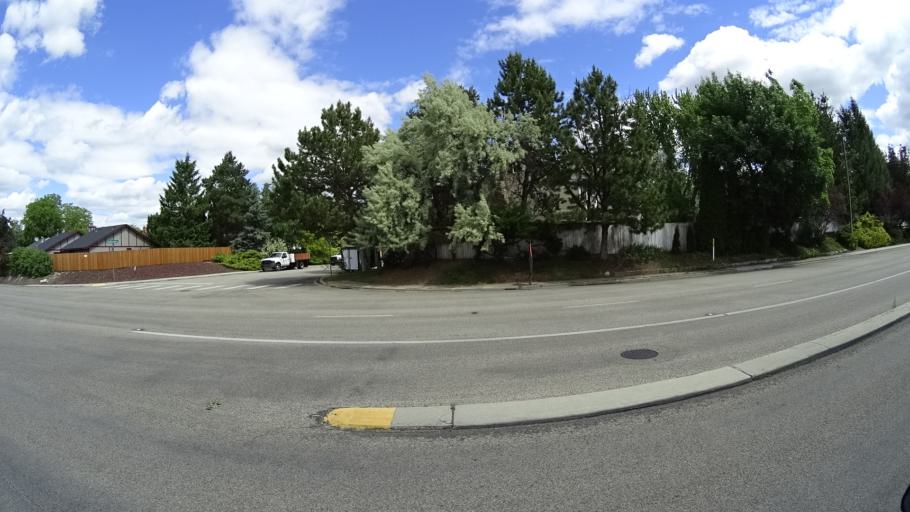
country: US
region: Idaho
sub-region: Ada County
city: Boise
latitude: 43.5822
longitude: -116.1686
